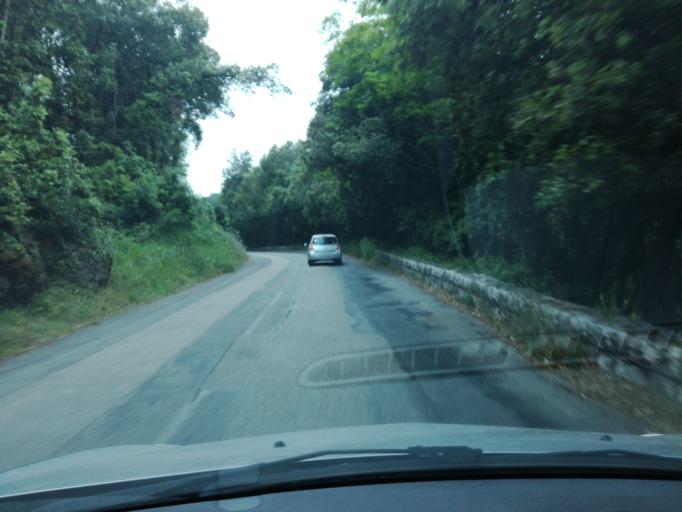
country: FR
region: Provence-Alpes-Cote d'Azur
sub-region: Departement des Alpes-Maritimes
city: Vallauris
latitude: 43.6052
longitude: 7.0656
